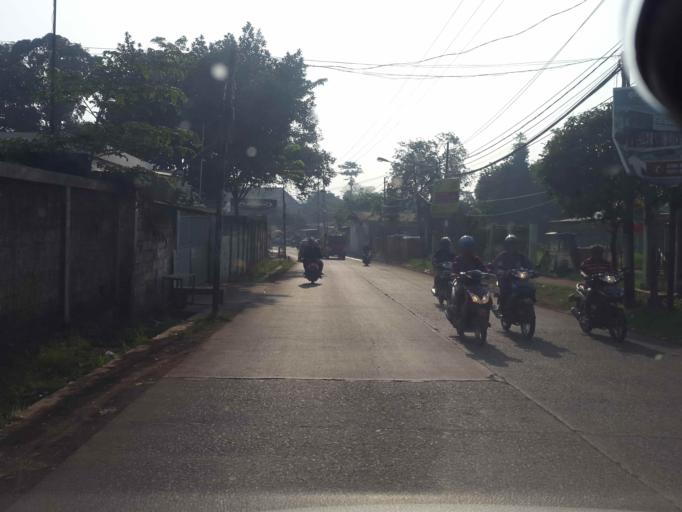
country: ID
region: West Java
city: Bekasi
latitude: -6.3154
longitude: 106.9995
